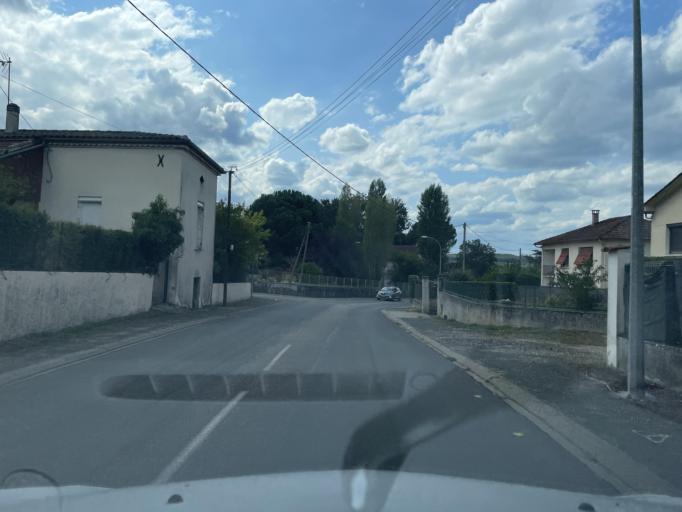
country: FR
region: Aquitaine
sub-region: Departement du Lot-et-Garonne
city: Casteljaloux
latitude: 44.3114
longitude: 0.0994
